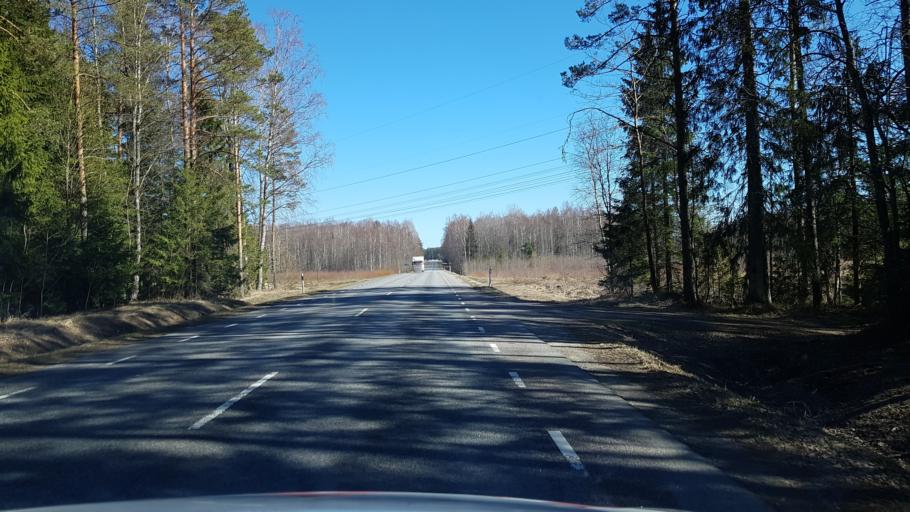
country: EE
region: Laeaene-Virumaa
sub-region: Viru-Nigula vald
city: Kunda
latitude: 59.3667
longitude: 26.6042
